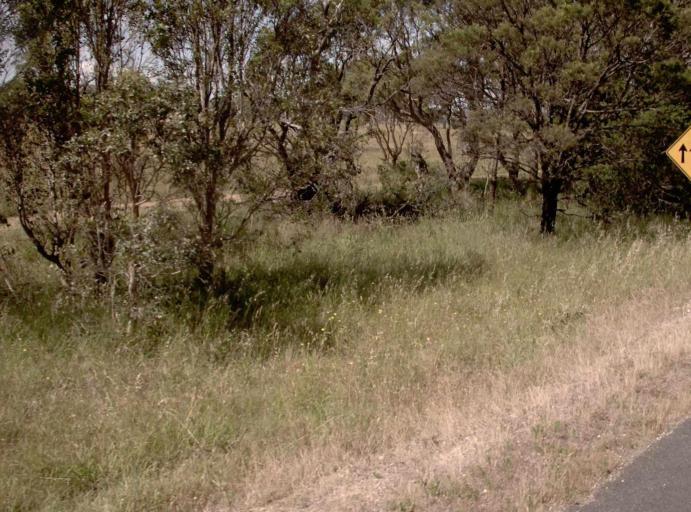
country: AU
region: Victoria
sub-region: East Gippsland
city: Bairnsdale
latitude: -37.8617
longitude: 147.5106
